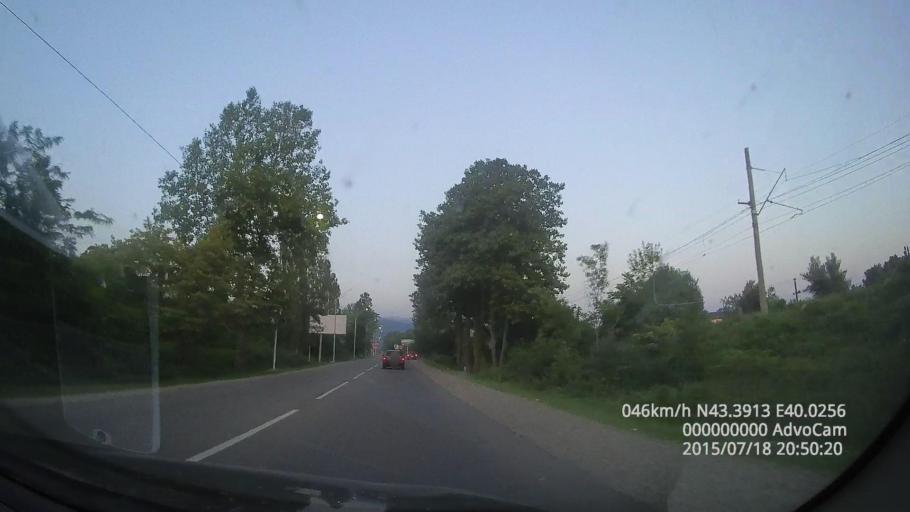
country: GE
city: Gantiadi
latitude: 43.3911
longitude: 40.0267
